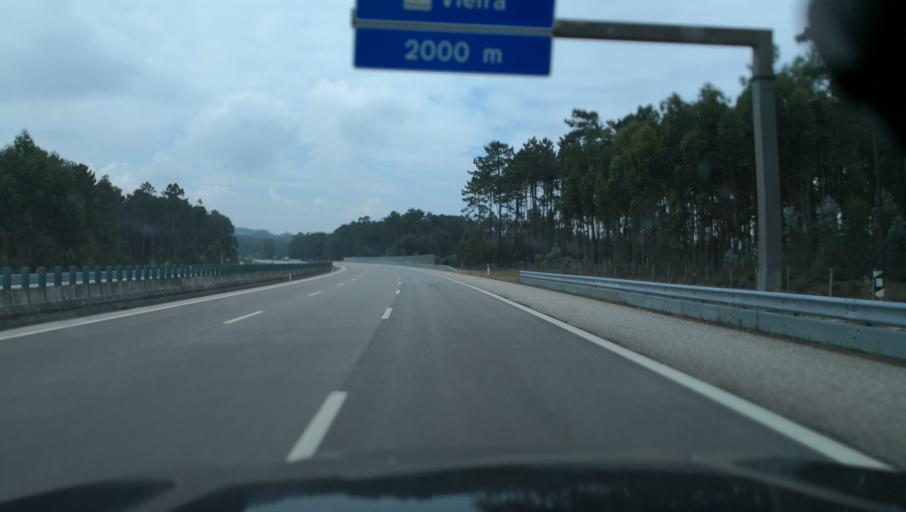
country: PT
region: Leiria
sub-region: Leiria
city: Monte Redondo
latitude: 39.8736
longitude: -8.8236
